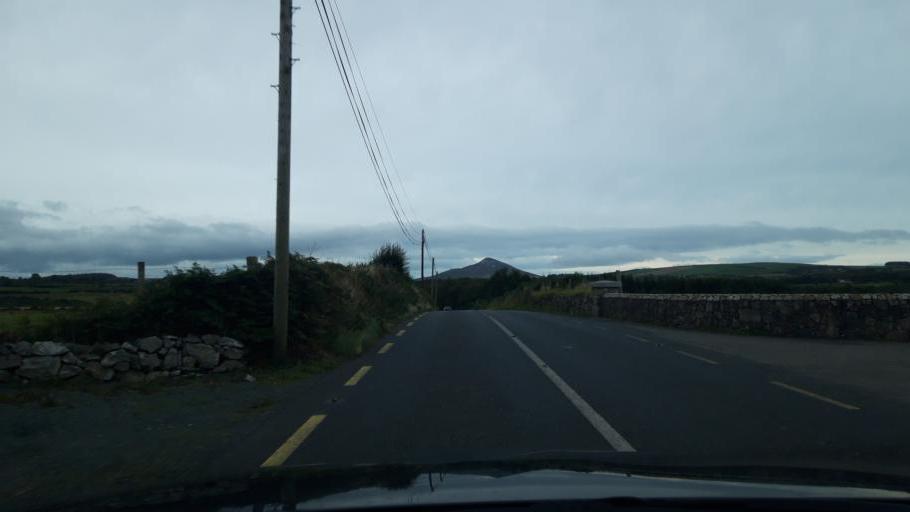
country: IE
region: Leinster
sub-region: Wicklow
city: Kilmacanoge
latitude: 53.1100
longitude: -6.1906
